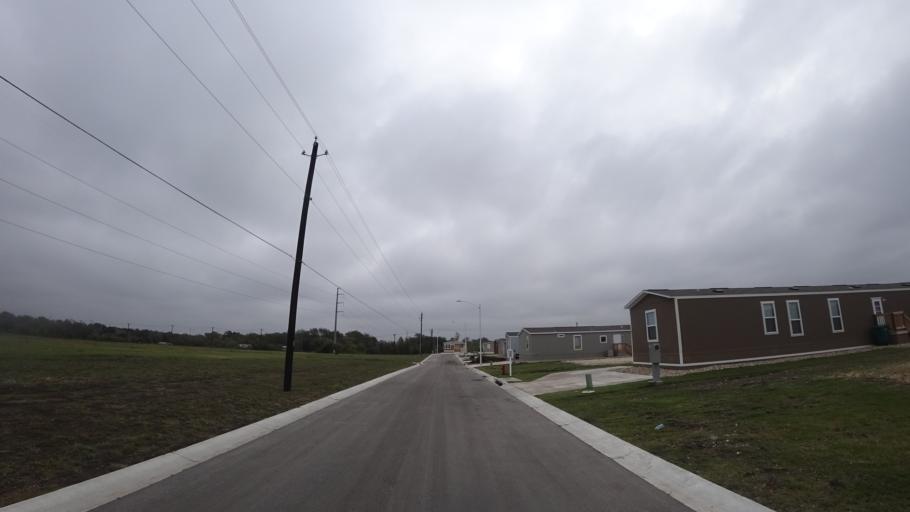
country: US
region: Texas
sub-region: Travis County
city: Pflugerville
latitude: 30.4084
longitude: -97.6050
